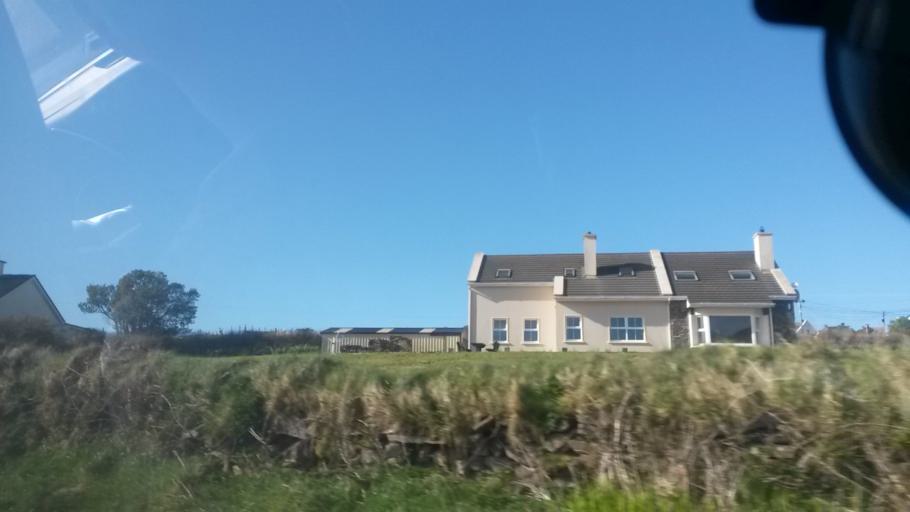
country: IE
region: Munster
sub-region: Ciarrai
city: Dingle
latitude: 52.1370
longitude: -10.4597
